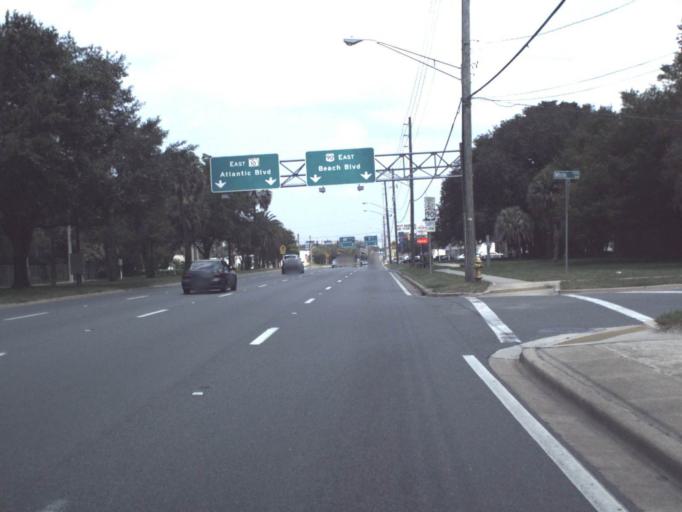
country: US
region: Florida
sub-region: Duval County
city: Jacksonville
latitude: 30.3064
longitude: -81.6395
